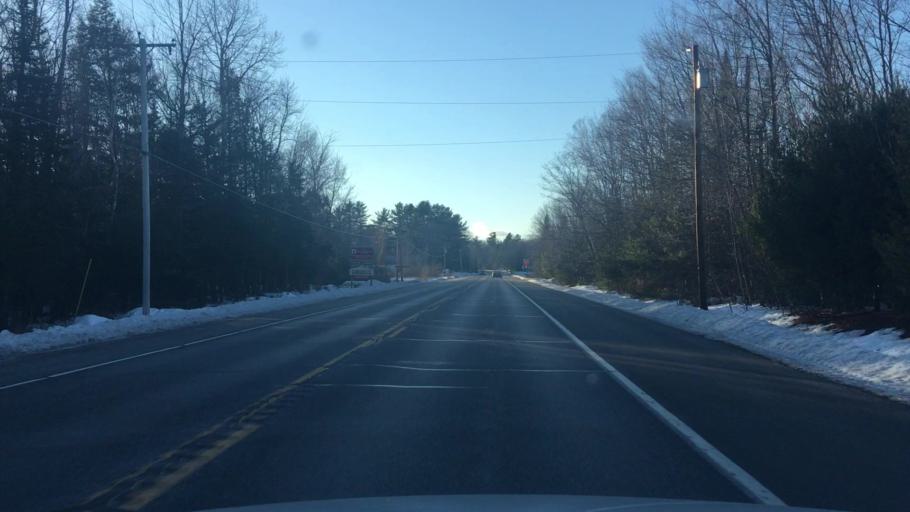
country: US
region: Maine
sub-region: Franklin County
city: New Sharon
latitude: 44.6781
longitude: -69.9191
